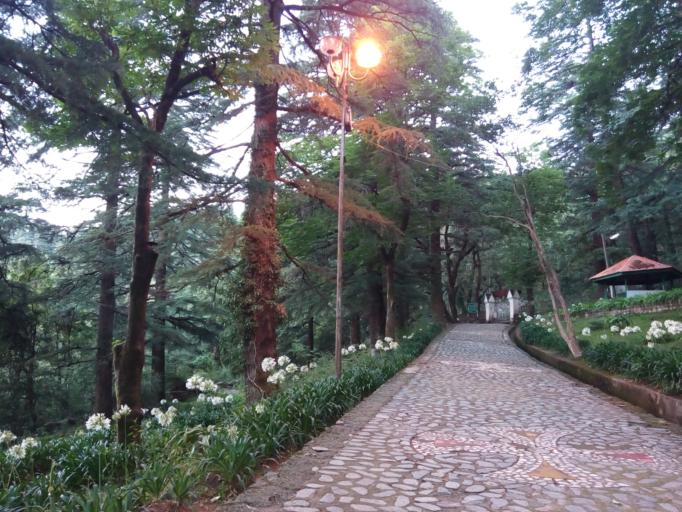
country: IN
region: Himachal Pradesh
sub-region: Kangra
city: Dharmsala
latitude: 32.2426
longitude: 76.3180
